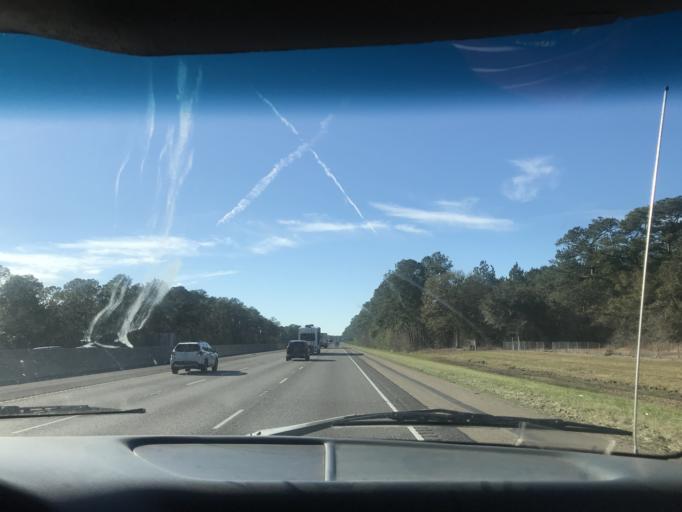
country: US
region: Louisiana
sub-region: Saint Tammany Parish
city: Slidell
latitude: 30.3103
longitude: -89.7954
